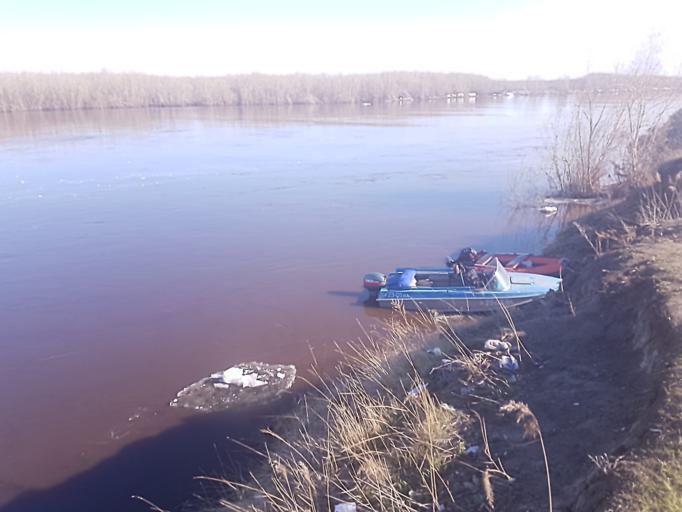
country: RU
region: Sakha
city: Yakutsk
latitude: 61.9715
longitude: 129.7002
